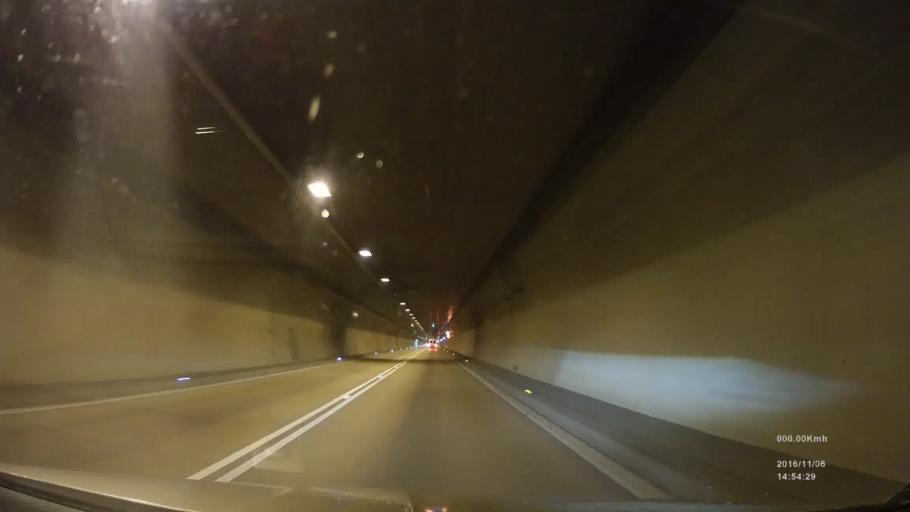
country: SK
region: Kosicky
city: Krompachy
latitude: 49.0033
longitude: 20.8766
